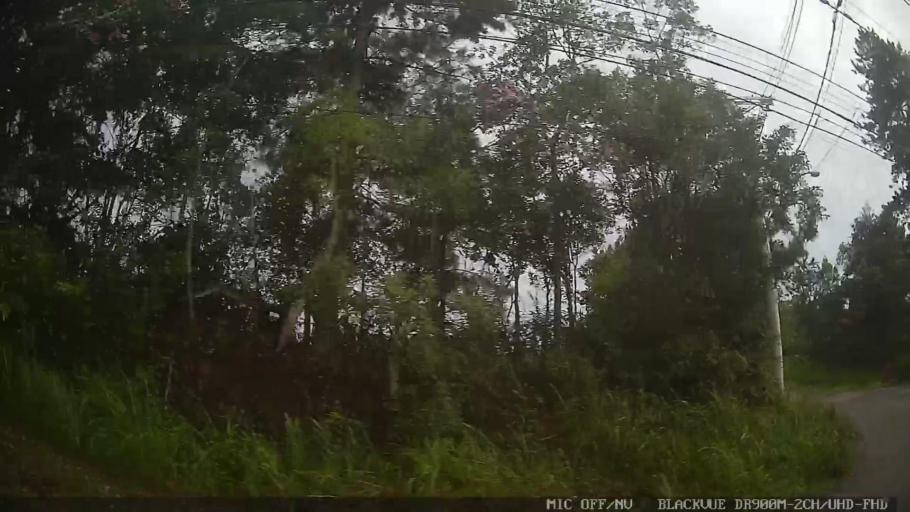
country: BR
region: Sao Paulo
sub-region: Ribeirao Pires
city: Ribeirao Pires
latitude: -23.6895
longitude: -46.3528
